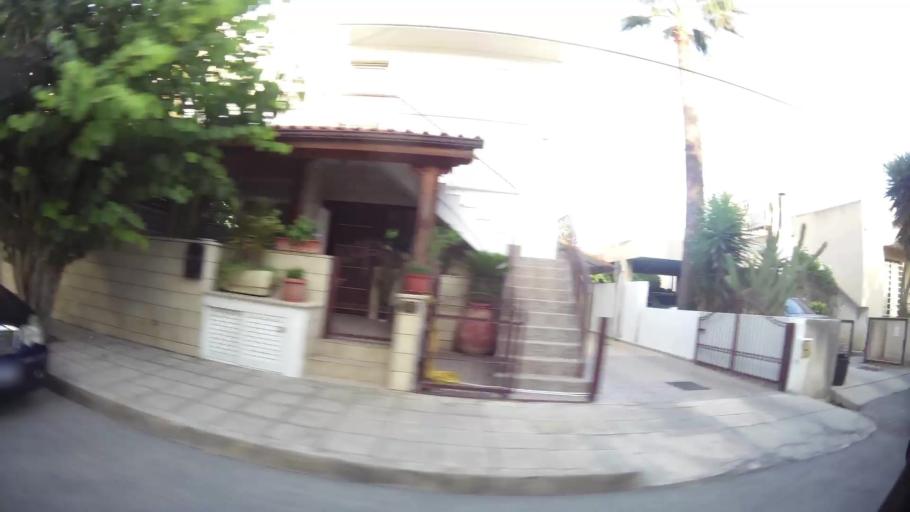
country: CY
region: Lefkosia
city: Nicosia
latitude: 35.1656
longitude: 33.3345
